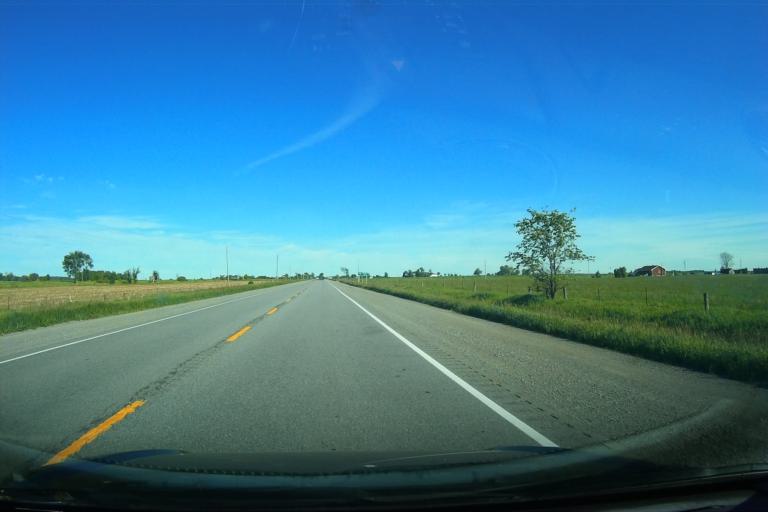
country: CA
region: Ontario
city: Pembroke
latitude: 45.6840
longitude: -76.9456
